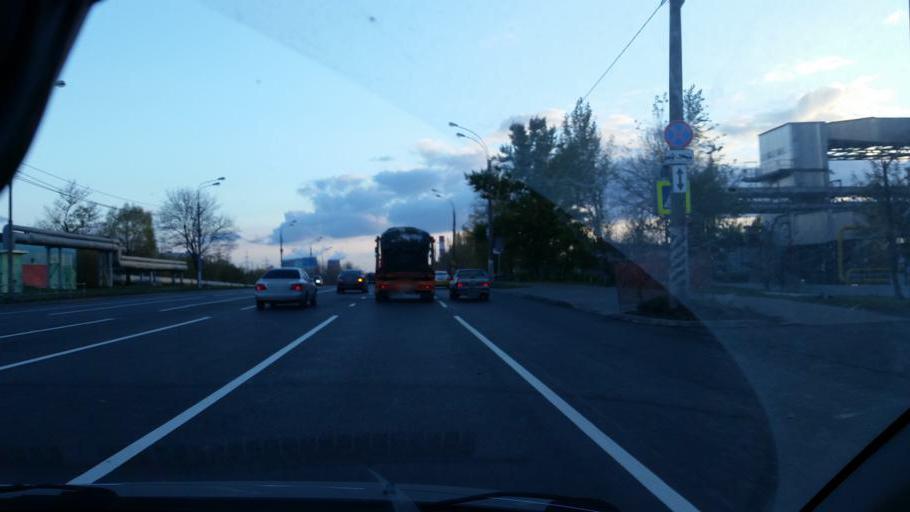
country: RU
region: Moskovskaya
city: Biryulevo Zapadnoye
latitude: 55.6002
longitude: 37.6367
